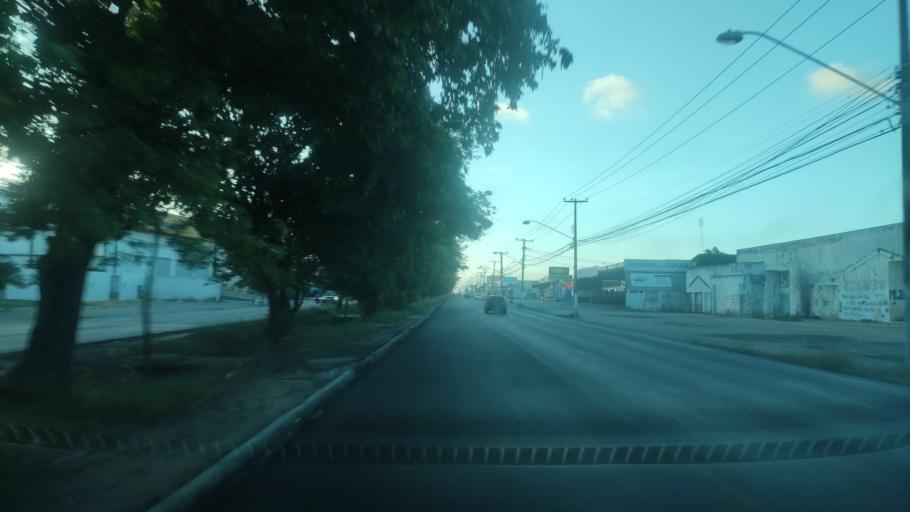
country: BR
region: Alagoas
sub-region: Satuba
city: Satuba
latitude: -9.5809
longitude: -35.7671
